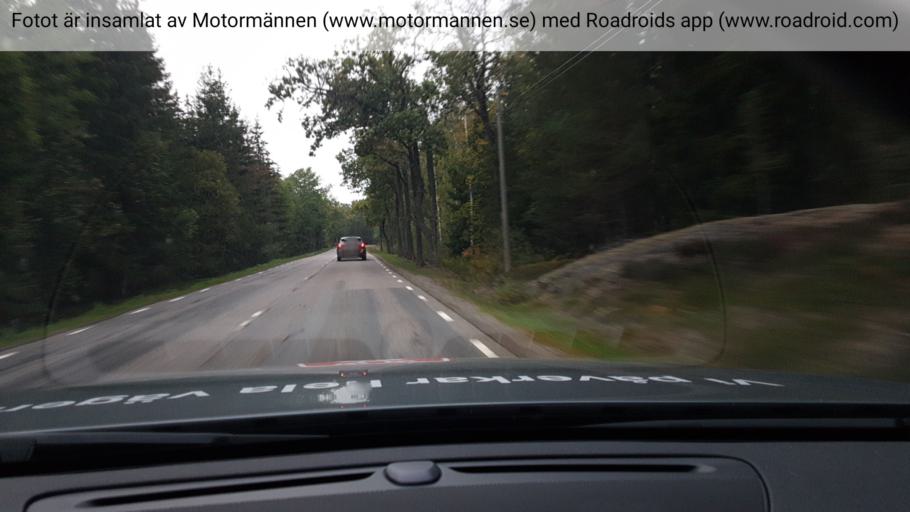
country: SE
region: Stockholm
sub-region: Haninge Kommun
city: Haninge
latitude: 59.1199
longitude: 18.1868
